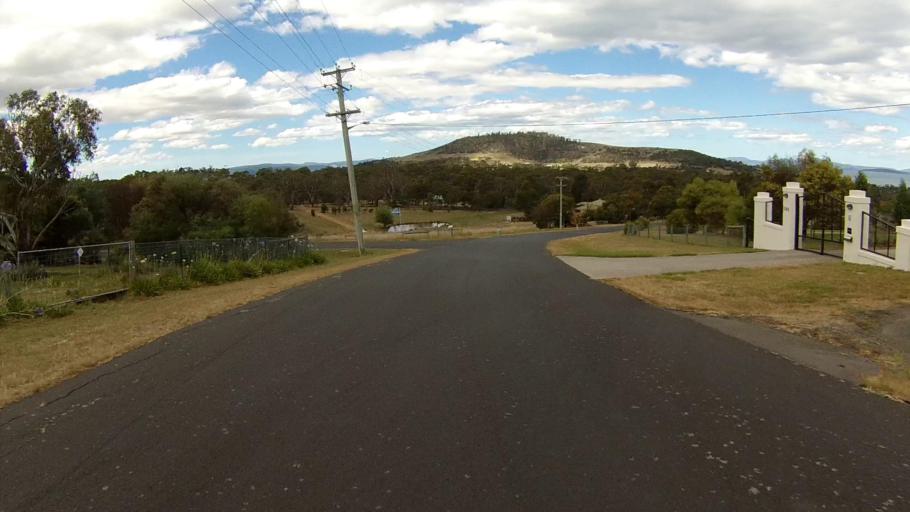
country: AU
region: Tasmania
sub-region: Clarence
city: Acton Park
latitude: -42.8812
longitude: 147.4717
